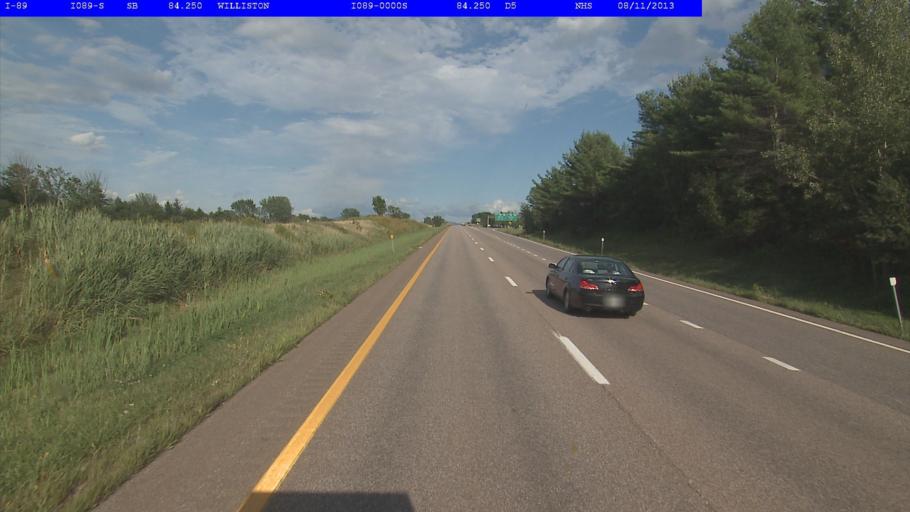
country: US
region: Vermont
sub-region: Chittenden County
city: Essex Junction
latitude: 44.4397
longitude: -73.1209
